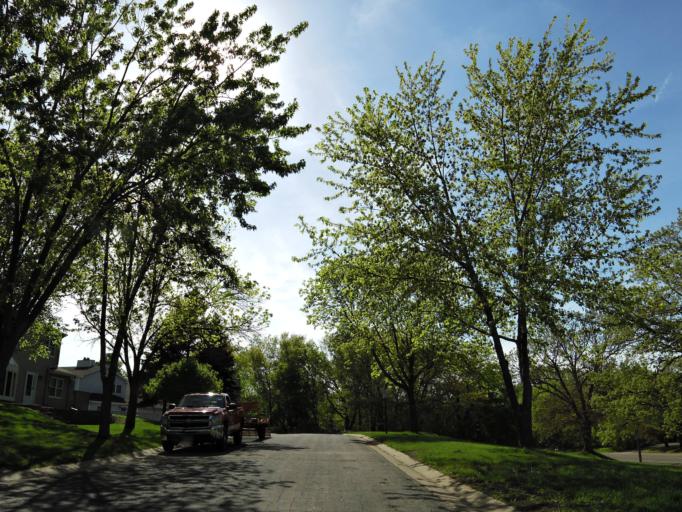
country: US
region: Minnesota
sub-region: Ramsey County
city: North Saint Paul
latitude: 45.0061
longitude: -92.9695
